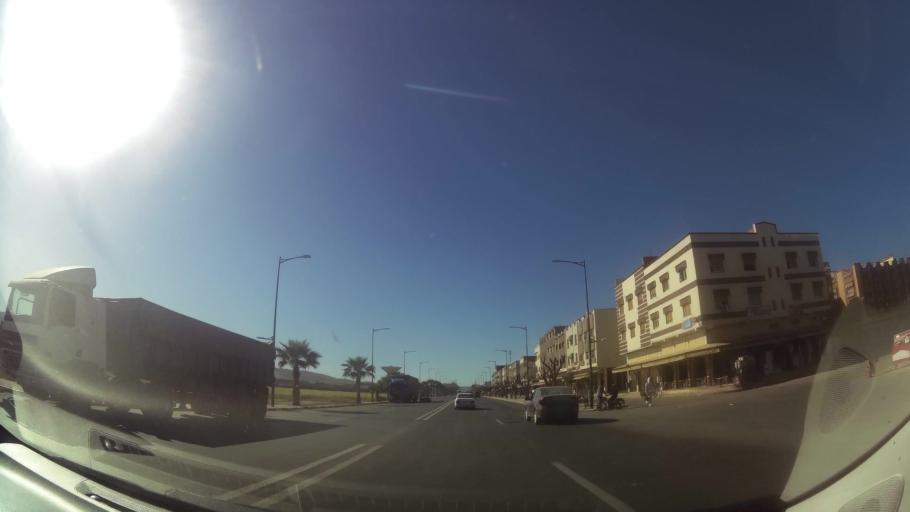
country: MA
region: Oriental
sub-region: Berkane-Taourirt
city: Ahfir
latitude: 34.8540
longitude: -1.9903
